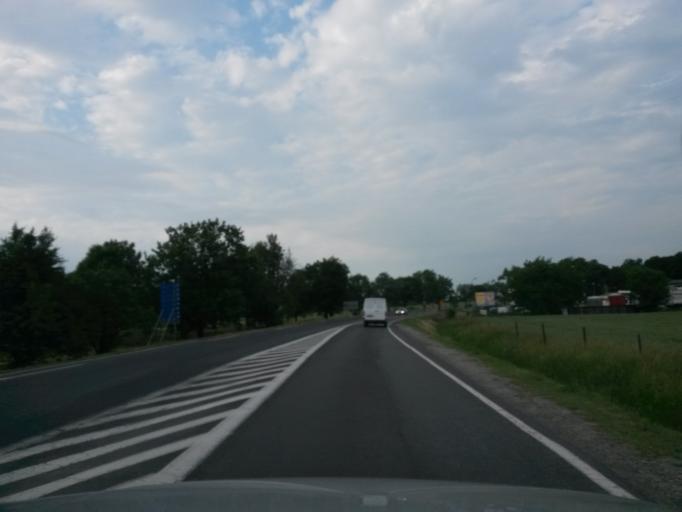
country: PL
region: Lower Silesian Voivodeship
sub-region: Powiat swidnicki
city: Strzegom
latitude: 50.9775
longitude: 16.3671
